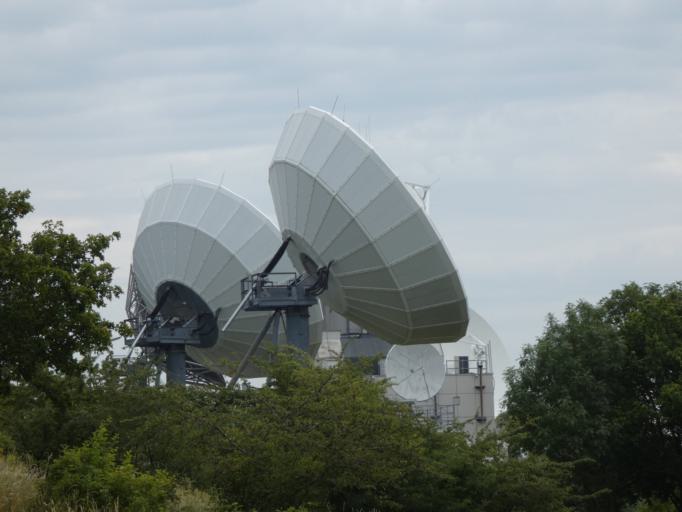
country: AT
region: Lower Austria
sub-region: Politischer Bezirk Bruck an der Leitha
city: Berg
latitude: 48.1149
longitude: 17.0234
